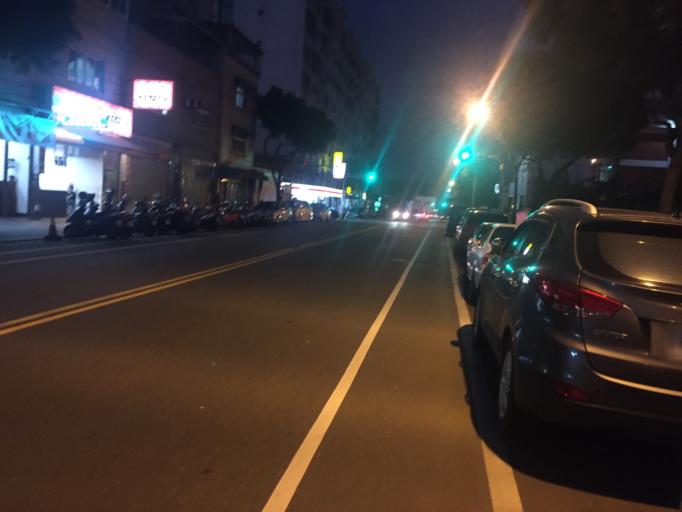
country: TW
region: Taiwan
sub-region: Taoyuan
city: Taoyuan
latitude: 24.9781
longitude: 121.3194
